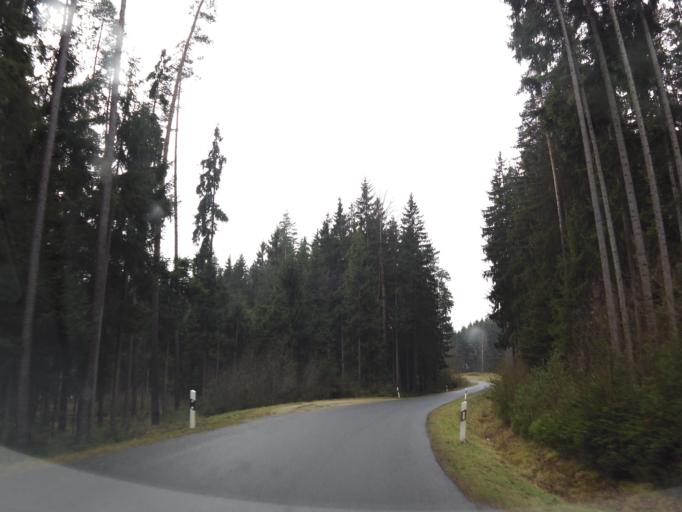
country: DE
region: Bavaria
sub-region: Upper Franconia
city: Wunsiedel
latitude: 50.0557
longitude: 12.0223
